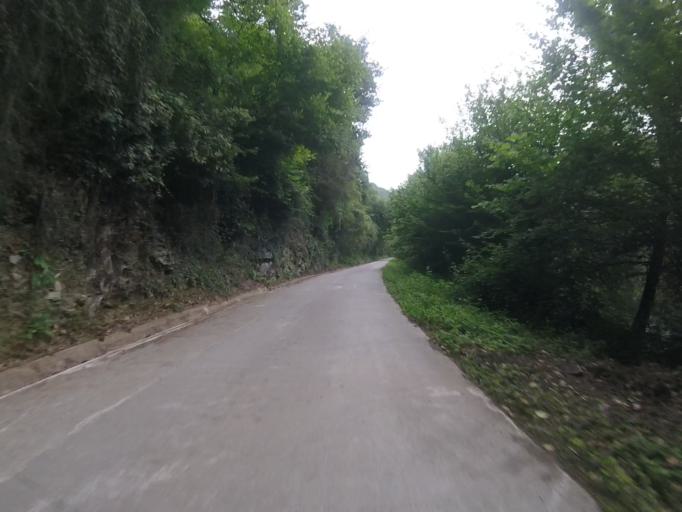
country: ES
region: Navarre
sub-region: Provincia de Navarra
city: Sunbilla
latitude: 43.1748
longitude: -1.6771
